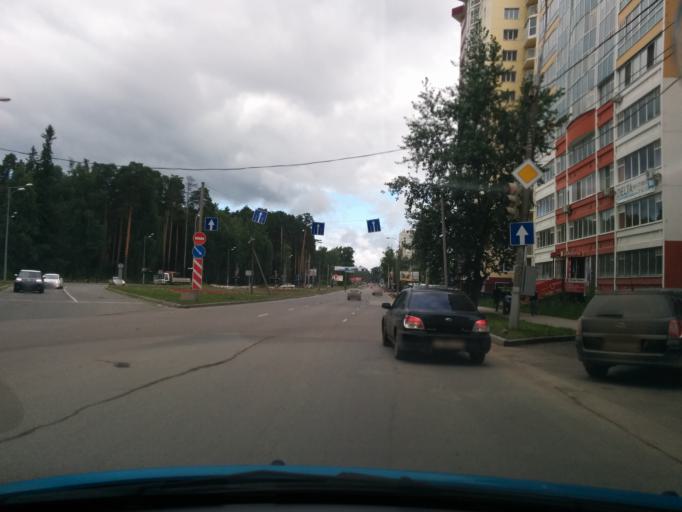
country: RU
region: Perm
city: Kondratovo
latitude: 58.0330
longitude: 56.0201
